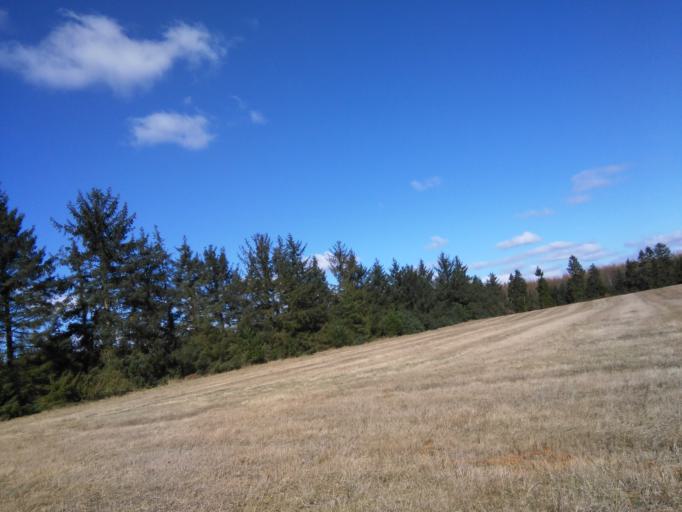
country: DK
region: Central Jutland
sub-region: Skanderborg Kommune
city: Ry
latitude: 56.0478
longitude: 9.7249
